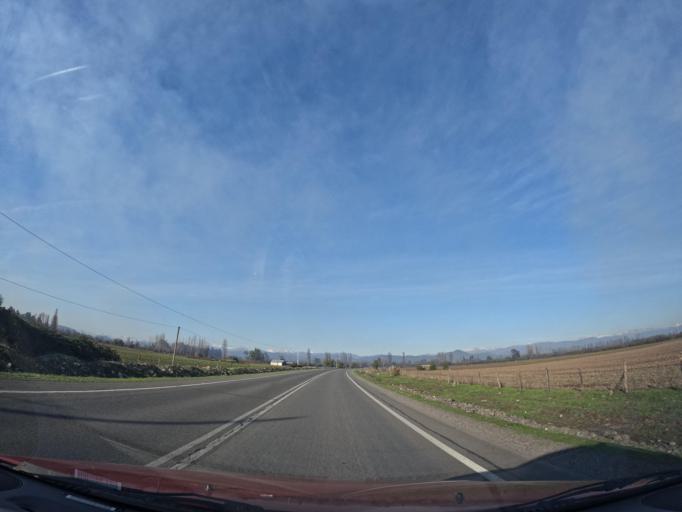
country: CL
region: Maule
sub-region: Provincia de Linares
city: Colbun
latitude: -35.6281
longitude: -71.4503
